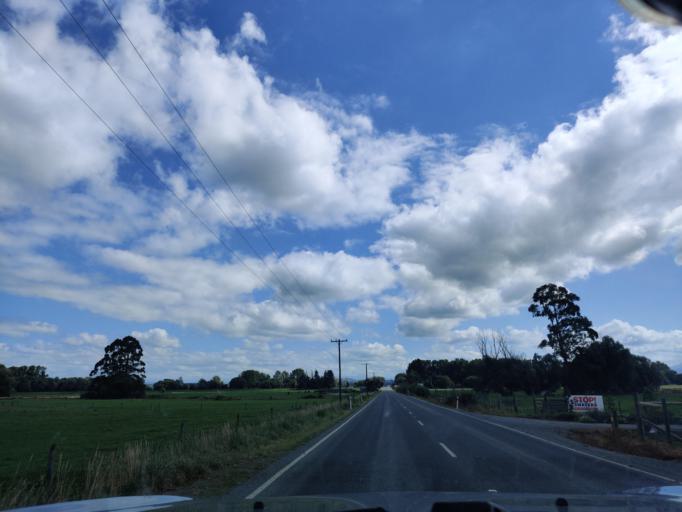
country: NZ
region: Canterbury
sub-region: Timaru District
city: Pleasant Point
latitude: -44.1265
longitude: 171.2657
